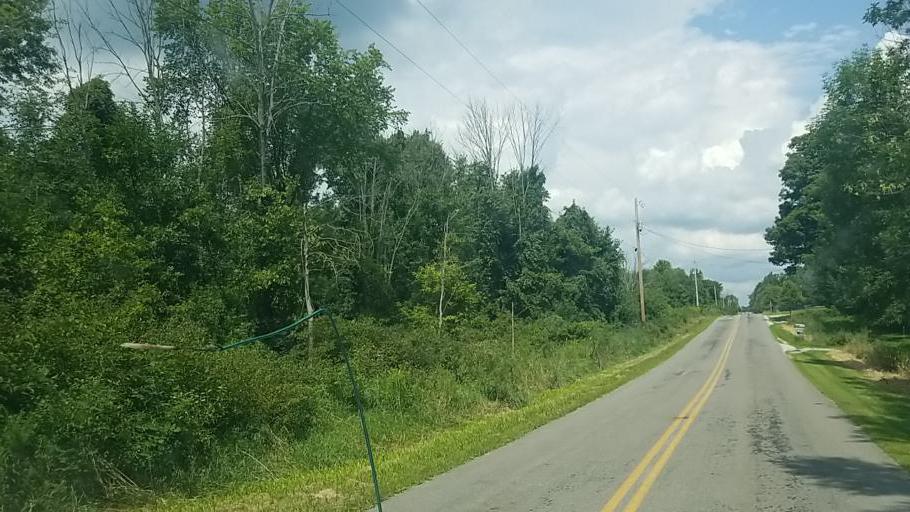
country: US
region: Ohio
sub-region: Medina County
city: Lodi
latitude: 41.1150
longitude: -82.0748
